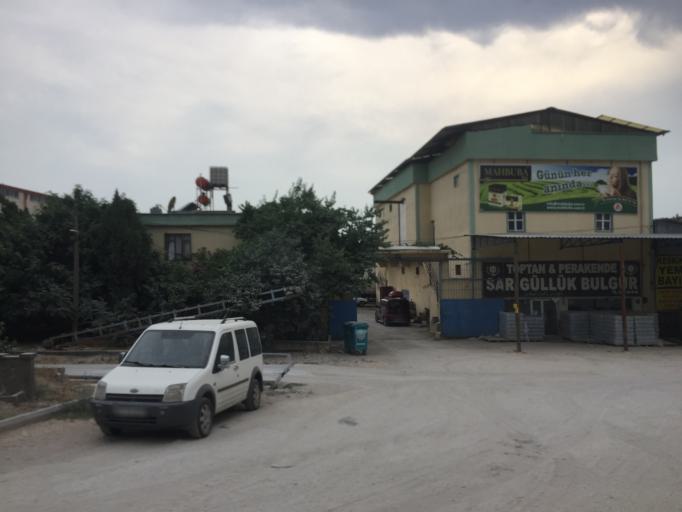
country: TR
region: Gaziantep
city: Gaziantep
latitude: 37.0207
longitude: 37.4288
